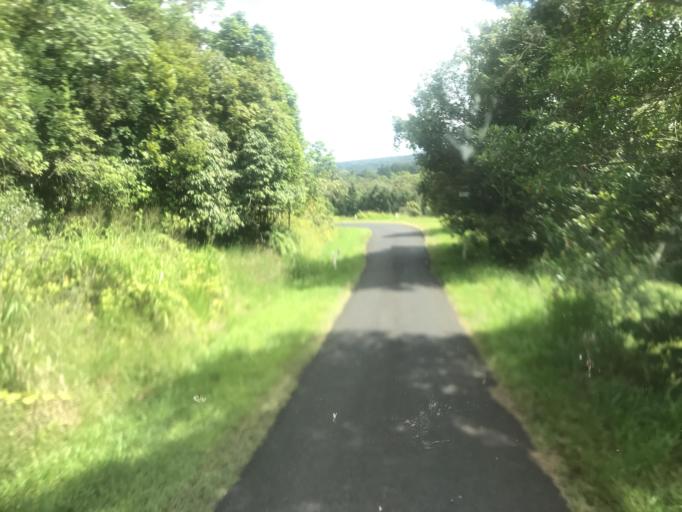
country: AU
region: Queensland
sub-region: Tablelands
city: Ravenshoe
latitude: -17.5434
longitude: 145.6922
